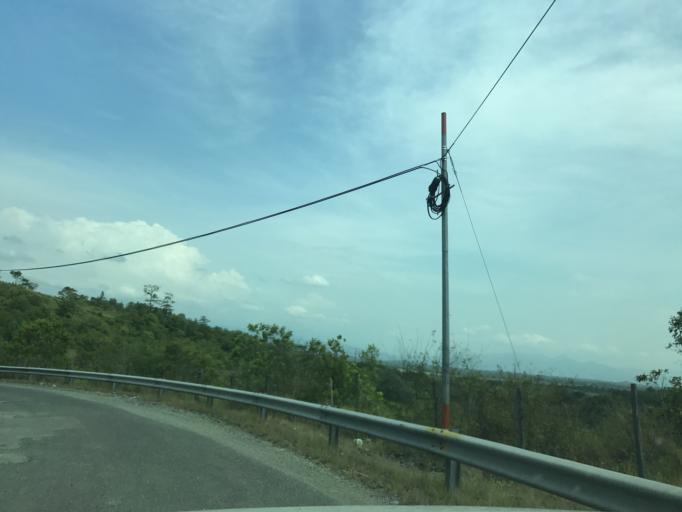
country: GT
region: Izabal
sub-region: Municipio de Los Amates
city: Los Amates
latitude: 15.3842
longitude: -89.0219
